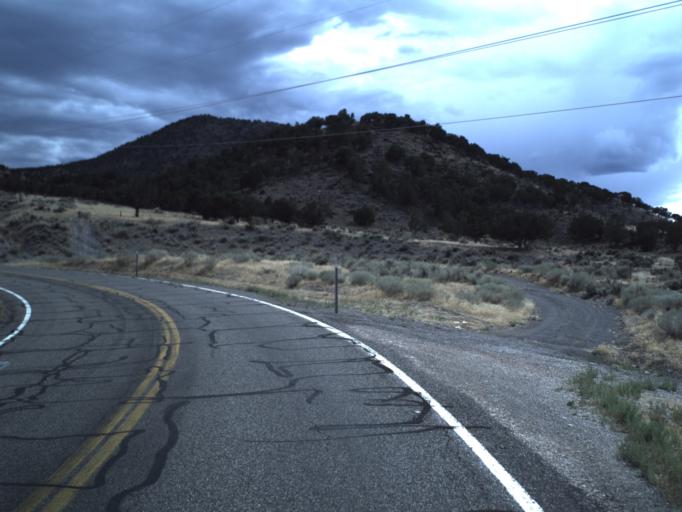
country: US
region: Utah
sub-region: Sevier County
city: Richfield
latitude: 38.7737
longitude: -111.9506
